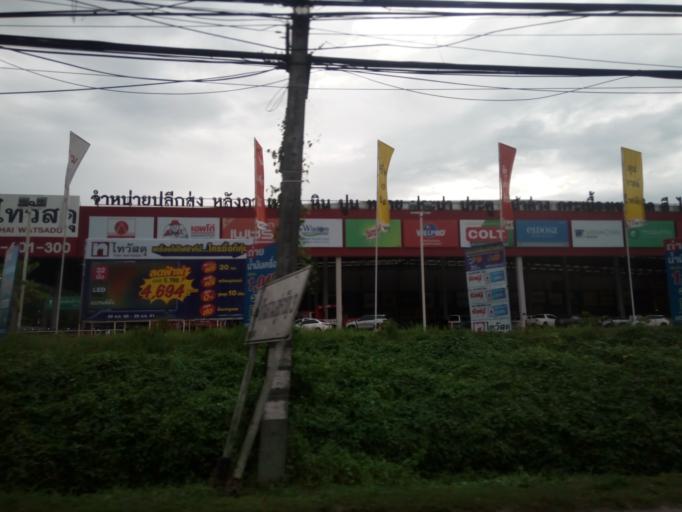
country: TH
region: Phuket
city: Thalang
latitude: 7.9859
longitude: 98.3588
